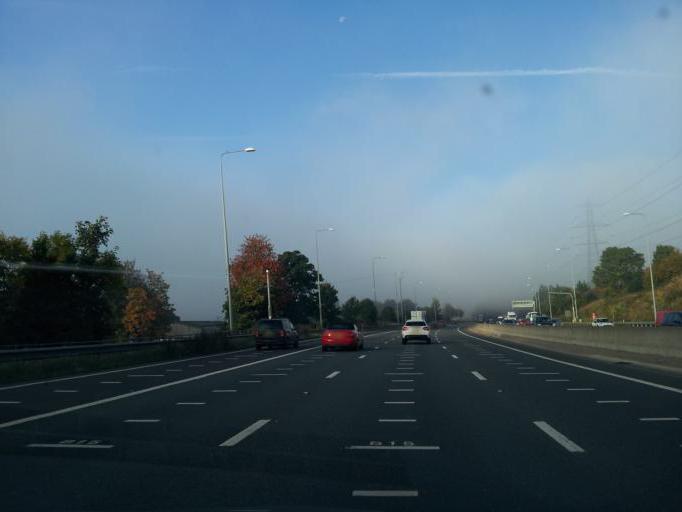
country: GB
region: England
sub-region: City and Borough of Leeds
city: Drighlington
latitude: 53.7411
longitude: -1.6827
